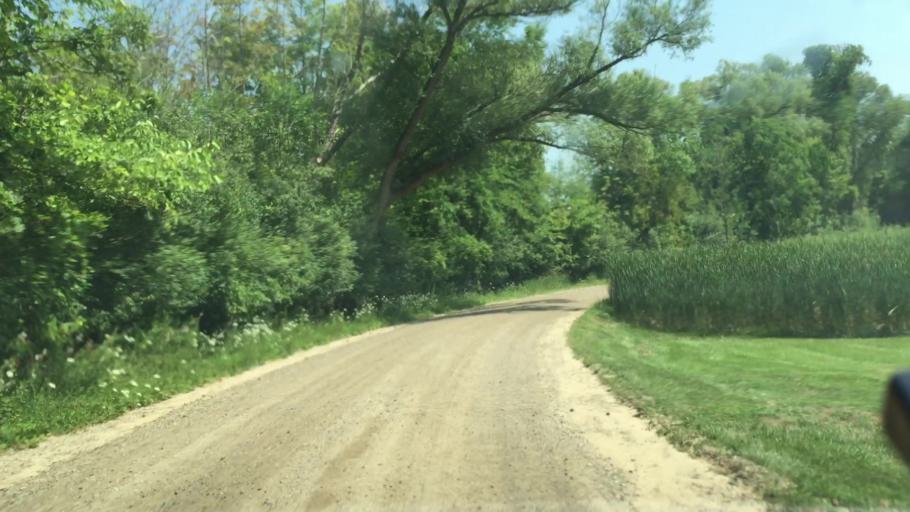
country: US
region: Michigan
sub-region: Oakland County
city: Franklin
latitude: 42.5492
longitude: -83.3321
